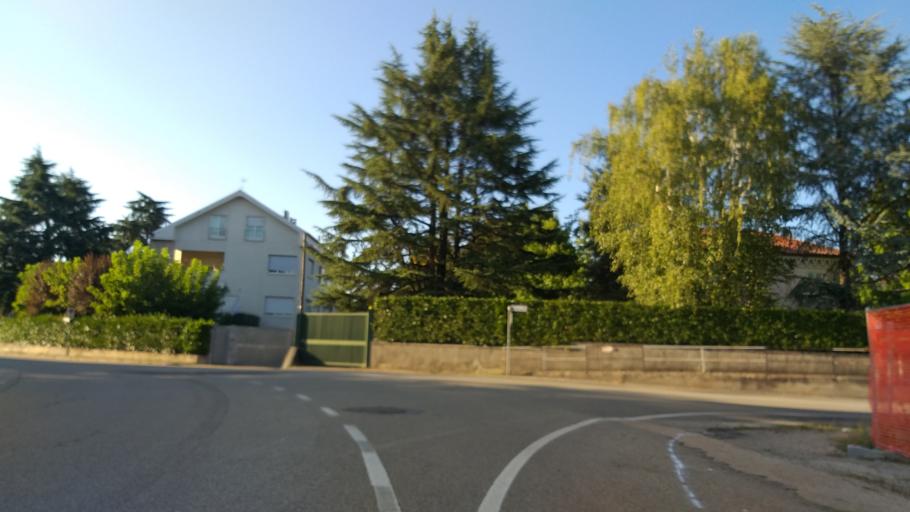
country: IT
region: Piedmont
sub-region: Provincia di Asti
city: Asti
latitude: 44.9099
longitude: 8.2071
